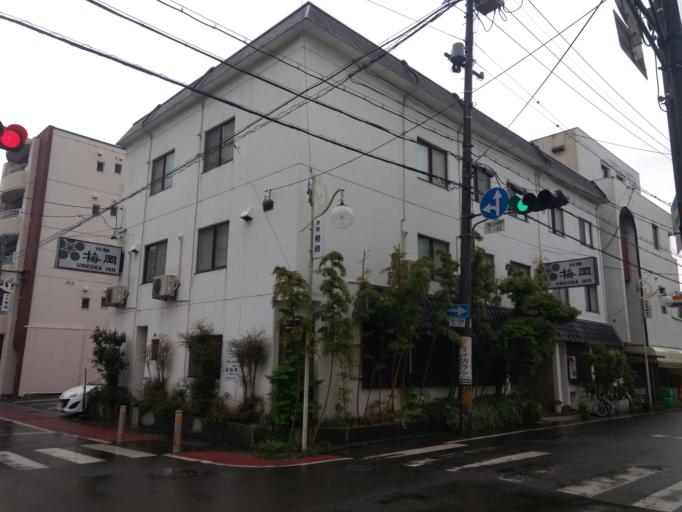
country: JP
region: Nagano
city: Nagano-shi
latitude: 36.6521
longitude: 138.1964
